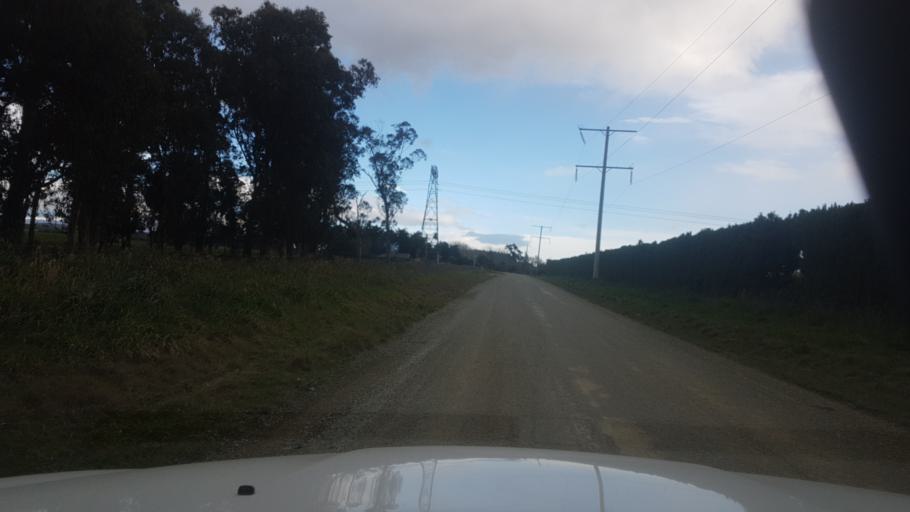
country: NZ
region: Canterbury
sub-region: Timaru District
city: Pleasant Point
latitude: -44.3536
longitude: 171.1323
